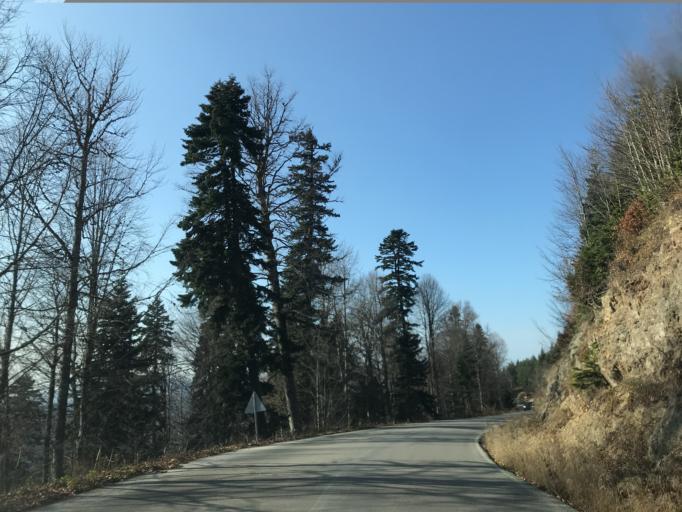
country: TR
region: Bolu
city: Bolu
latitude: 40.8874
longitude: 31.6802
